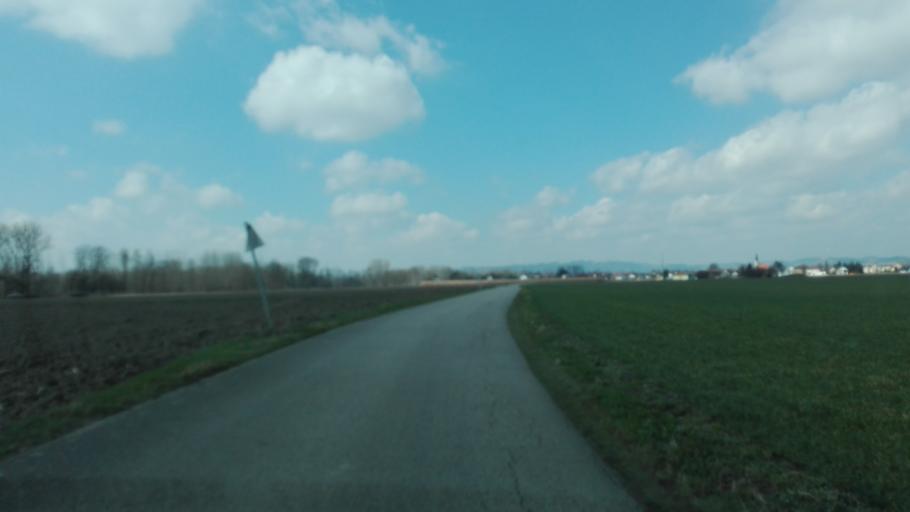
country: AT
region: Upper Austria
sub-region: Politischer Bezirk Urfahr-Umgebung
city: Goldworth
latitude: 48.3210
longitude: 14.1132
